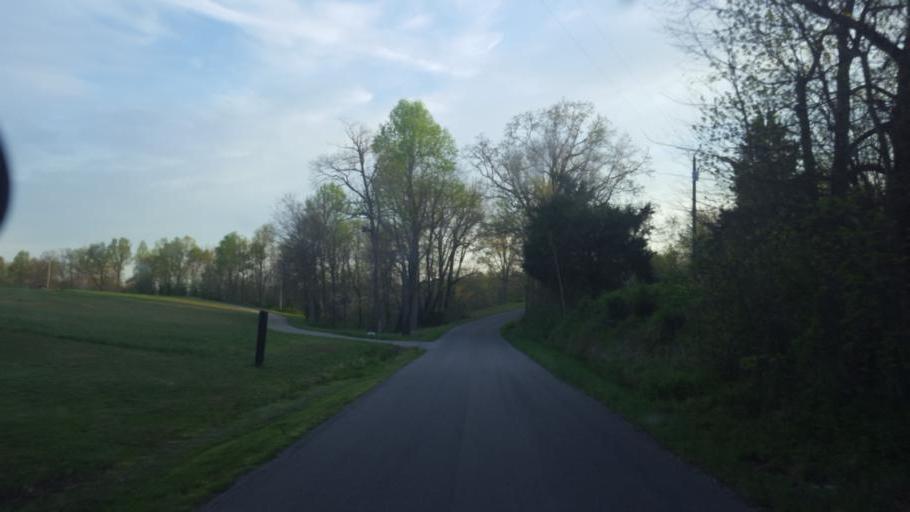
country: US
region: Kentucky
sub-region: Barren County
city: Cave City
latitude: 37.1401
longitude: -86.0252
